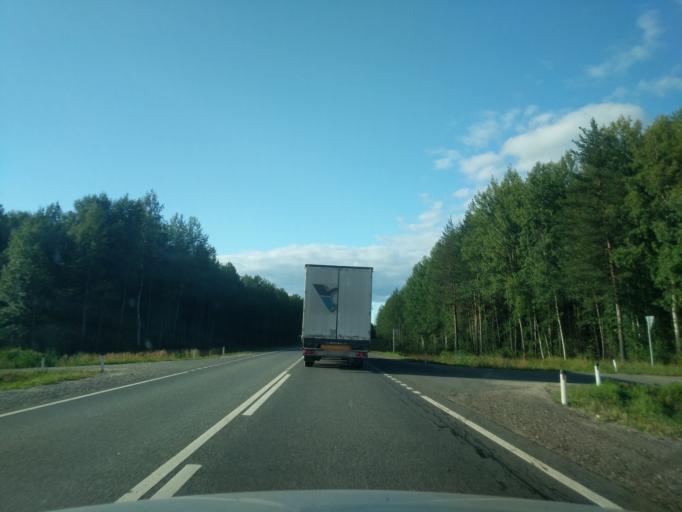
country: RU
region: Kostroma
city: Manturovo
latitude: 58.3132
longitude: 44.7205
